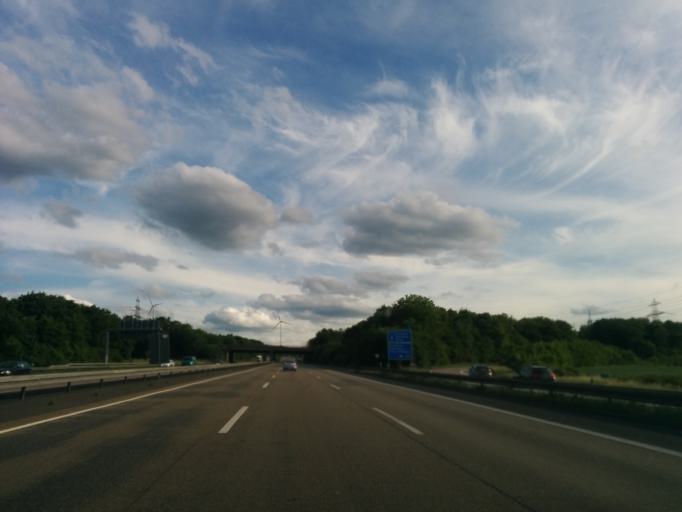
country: DE
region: Hesse
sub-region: Regierungsbezirk Kassel
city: Lohfelden
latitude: 51.2637
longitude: 9.5164
